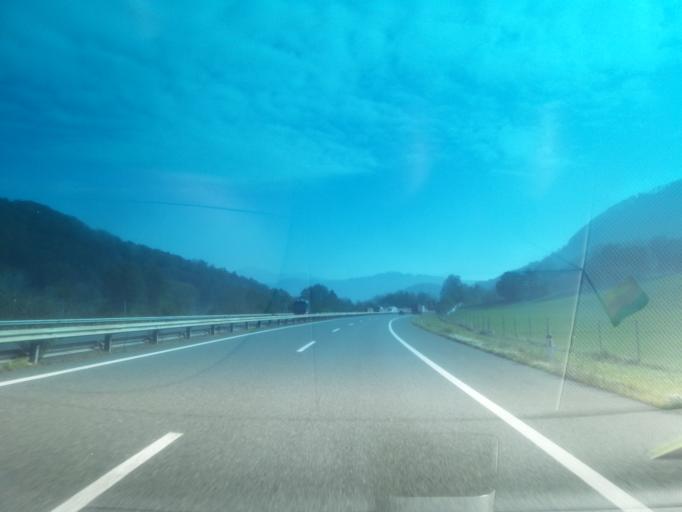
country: AT
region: Styria
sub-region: Politischer Bezirk Graz-Umgebung
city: Deutschfeistritz
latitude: 47.2171
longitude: 15.3032
